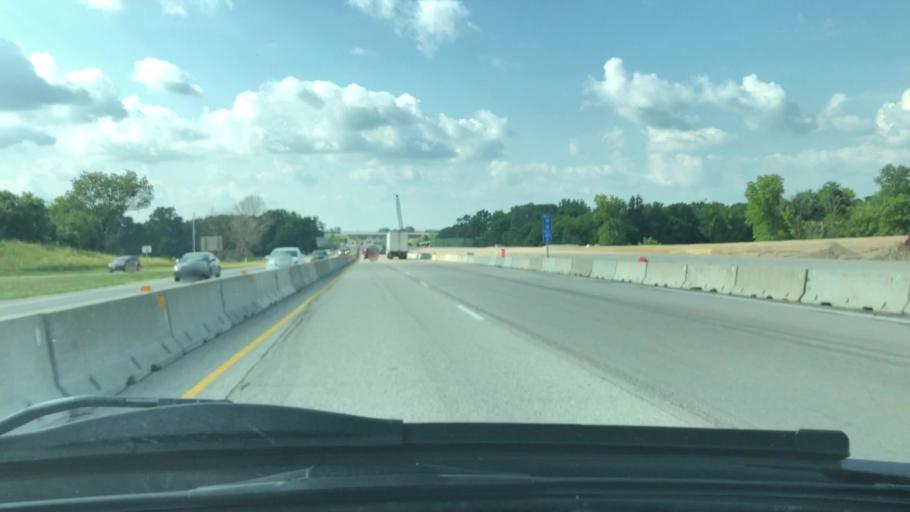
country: US
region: Wisconsin
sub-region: Rock County
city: Beloit
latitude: 42.5619
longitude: -88.9781
